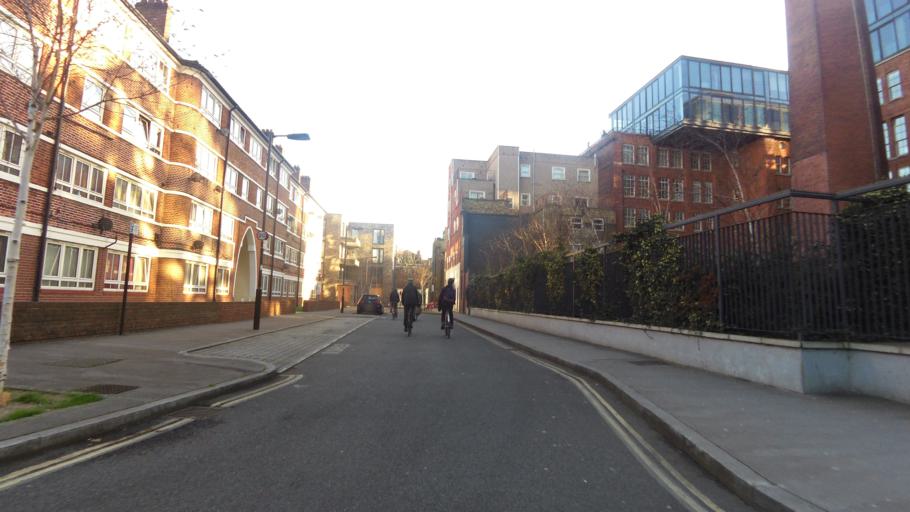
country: GB
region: England
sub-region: Greater London
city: City of London
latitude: 51.4966
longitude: -0.0841
